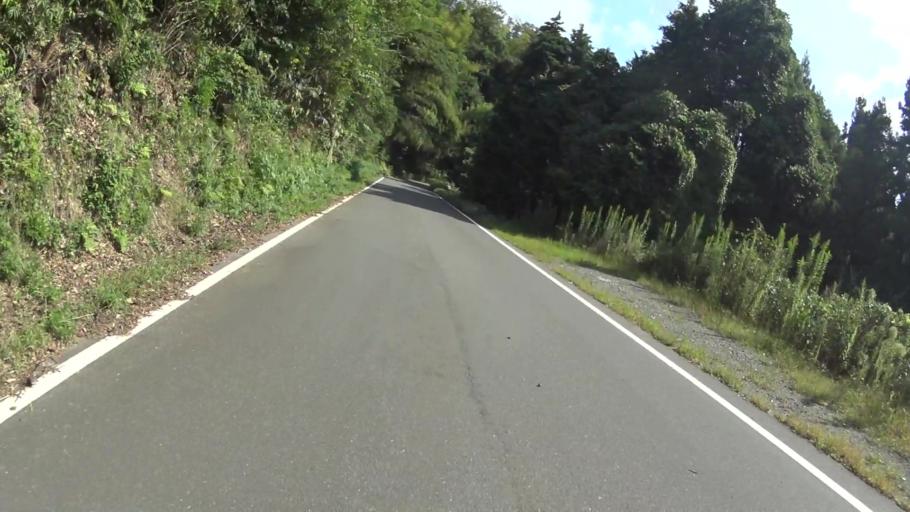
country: JP
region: Kyoto
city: Miyazu
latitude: 35.6294
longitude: 135.2284
